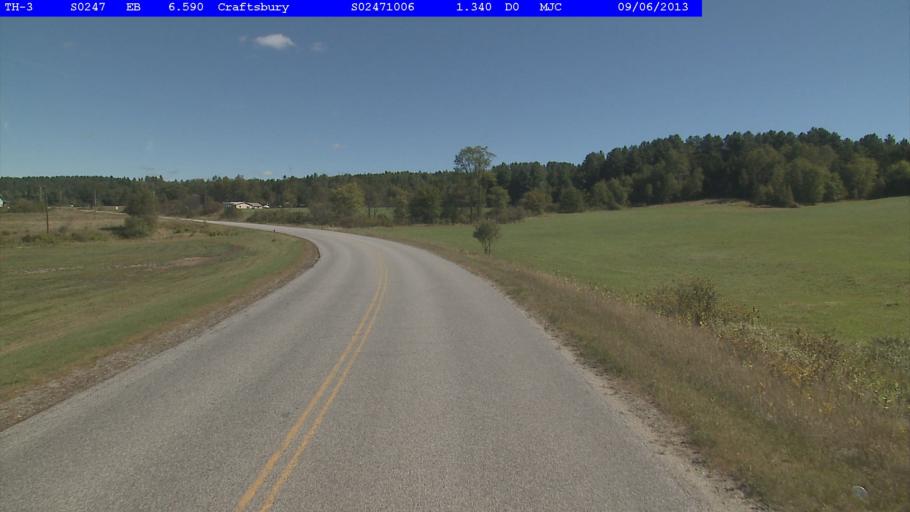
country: US
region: Vermont
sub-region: Caledonia County
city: Hardwick
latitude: 44.6317
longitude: -72.4242
